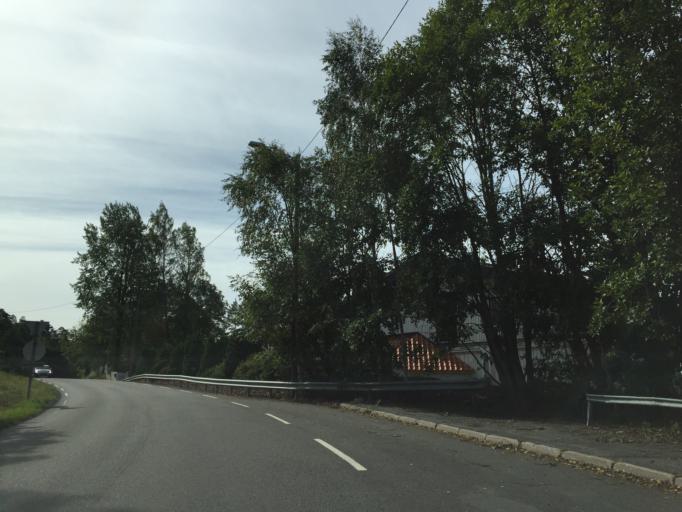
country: NO
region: Ostfold
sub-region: Moss
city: Moss
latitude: 59.5117
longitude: 10.6853
